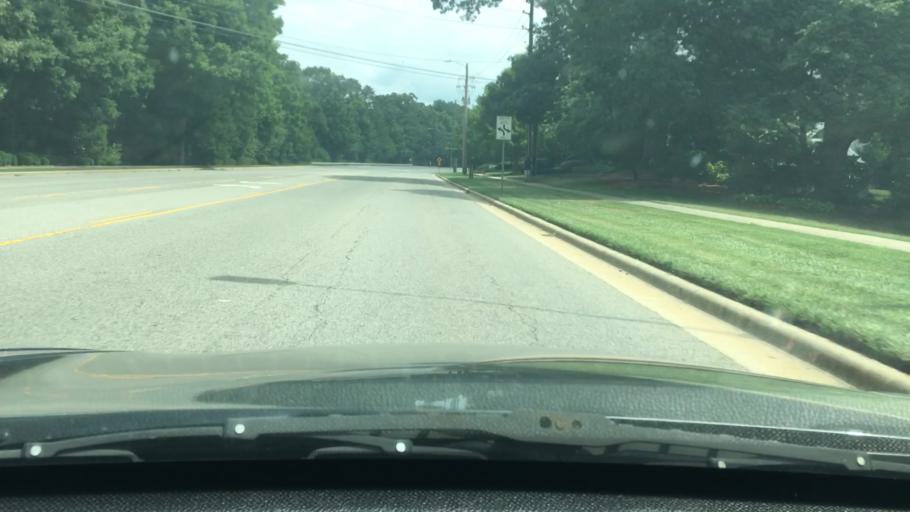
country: US
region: North Carolina
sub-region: Wake County
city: West Raleigh
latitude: 35.8333
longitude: -78.7117
